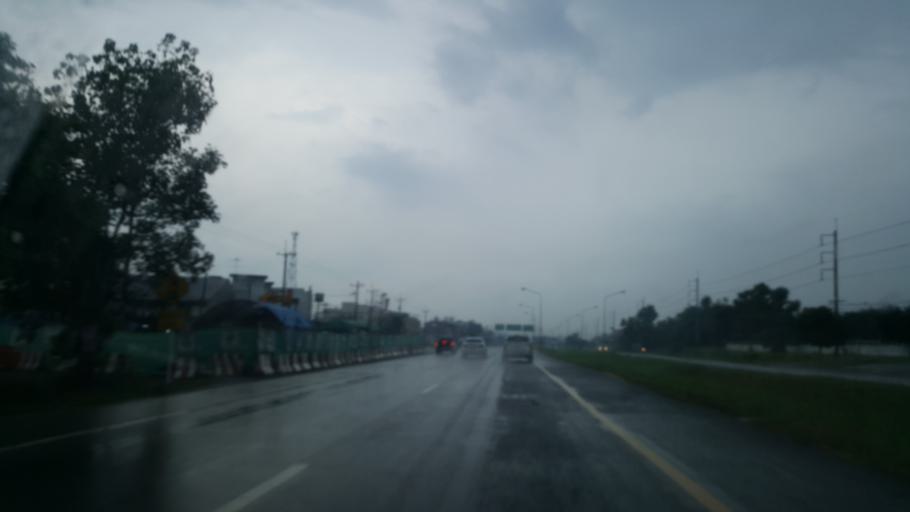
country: TH
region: Chon Buri
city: Ban Talat Bueng
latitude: 12.9553
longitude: 101.0487
